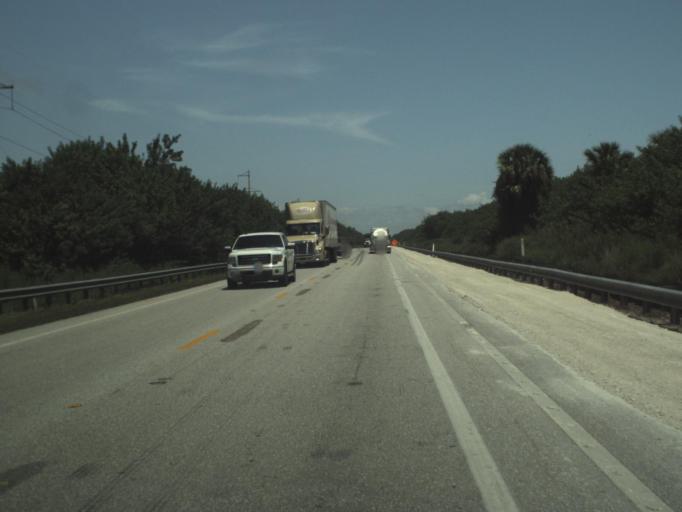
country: US
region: Florida
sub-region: Okeechobee County
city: Taylor Creek
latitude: 27.1343
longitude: -80.6400
